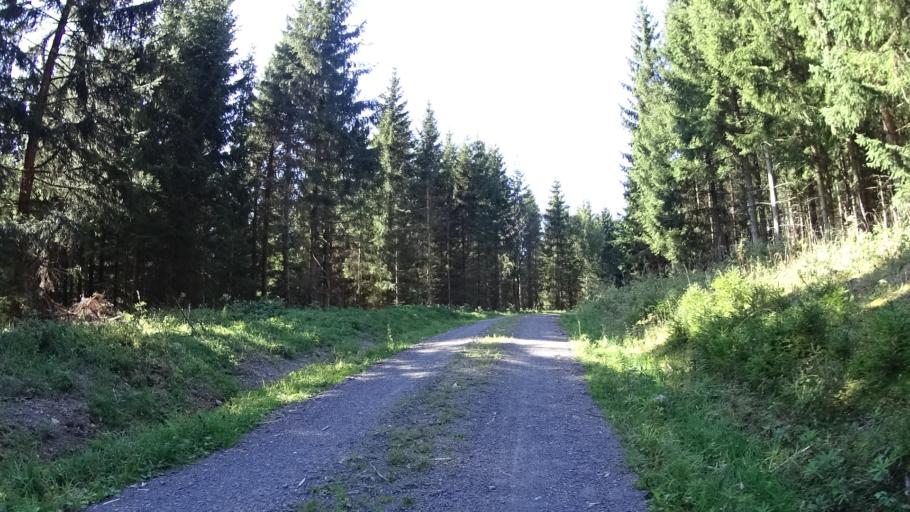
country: DE
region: Thuringia
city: Neuhaus
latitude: 50.6363
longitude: 10.9277
